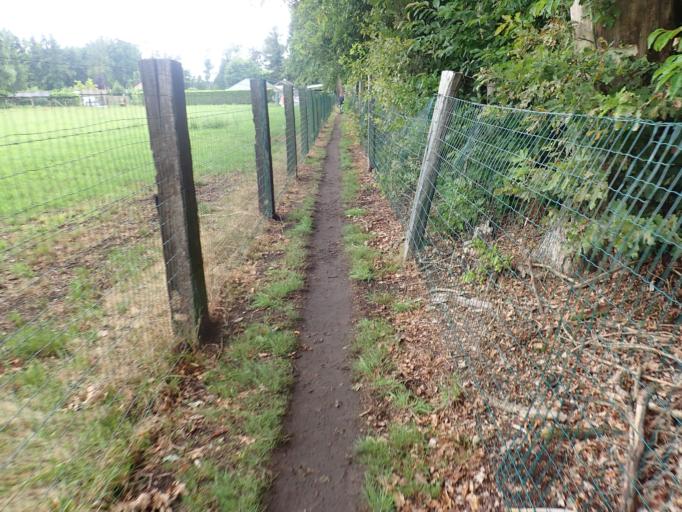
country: BE
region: Flanders
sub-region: Provincie Antwerpen
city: Lille
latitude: 51.2711
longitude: 4.8061
